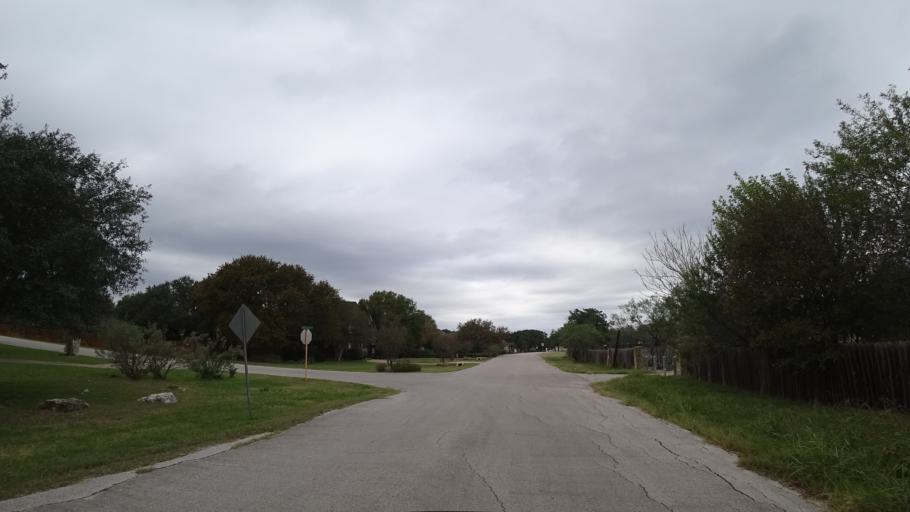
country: US
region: Texas
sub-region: Travis County
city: Shady Hollow
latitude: 30.1522
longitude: -97.8623
